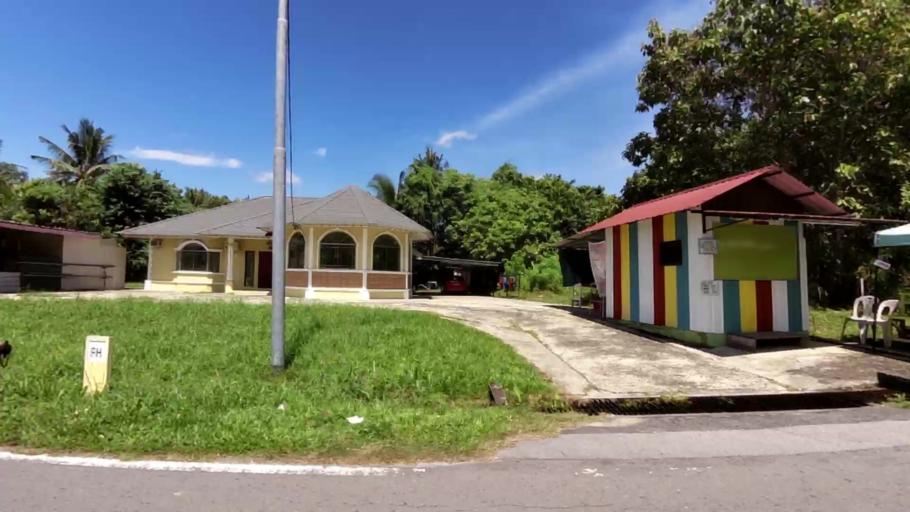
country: BN
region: Brunei and Muara
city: Bandar Seri Begawan
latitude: 4.9408
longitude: 114.9495
